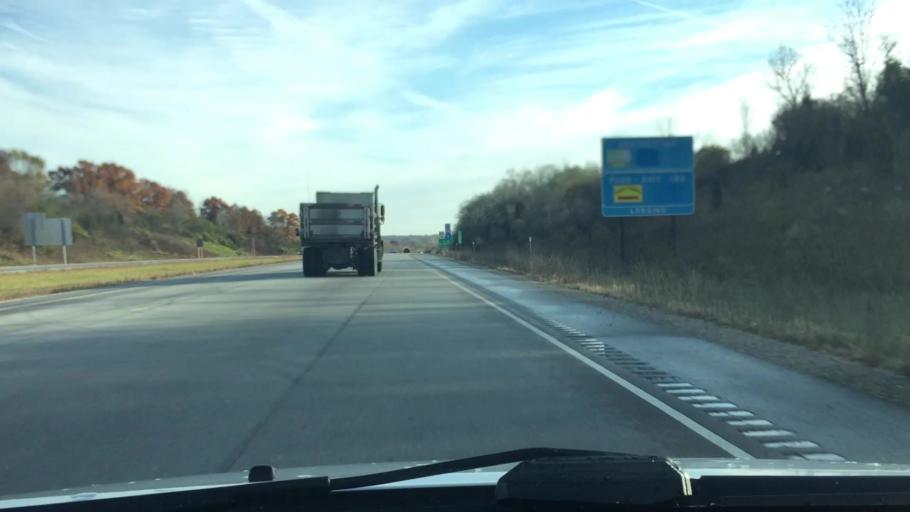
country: US
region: Wisconsin
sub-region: Waukesha County
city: Hartland
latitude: 43.1072
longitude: -88.3571
